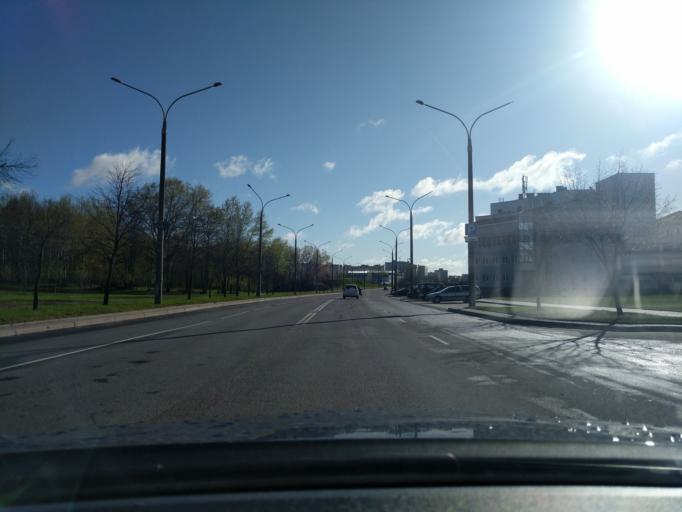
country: BY
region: Minsk
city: Novoye Medvezhino
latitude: 53.9009
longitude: 27.4678
